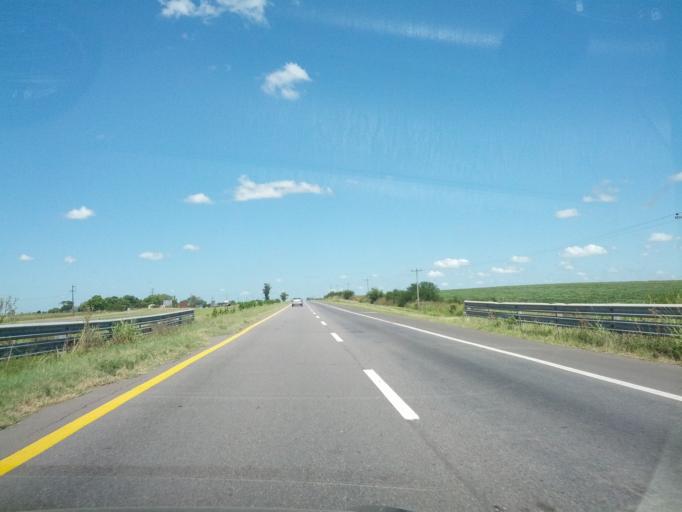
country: AR
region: Entre Rios
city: Gualeguaychu
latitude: -33.0796
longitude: -58.6354
